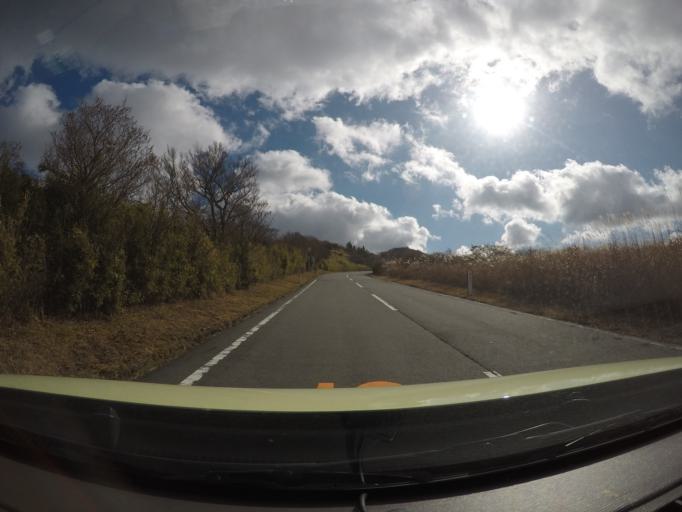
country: JP
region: Kanagawa
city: Hakone
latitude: 35.2050
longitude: 138.9864
